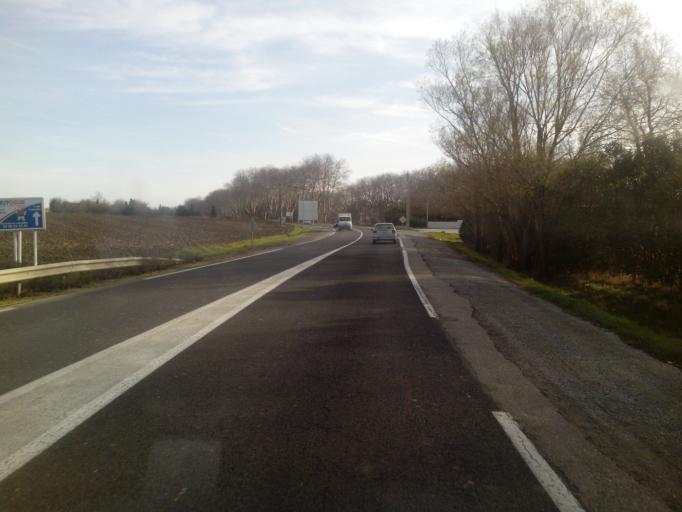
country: FR
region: Languedoc-Roussillon
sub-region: Departement de l'Aude
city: Castelnaudary
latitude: 43.3052
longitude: 1.9808
